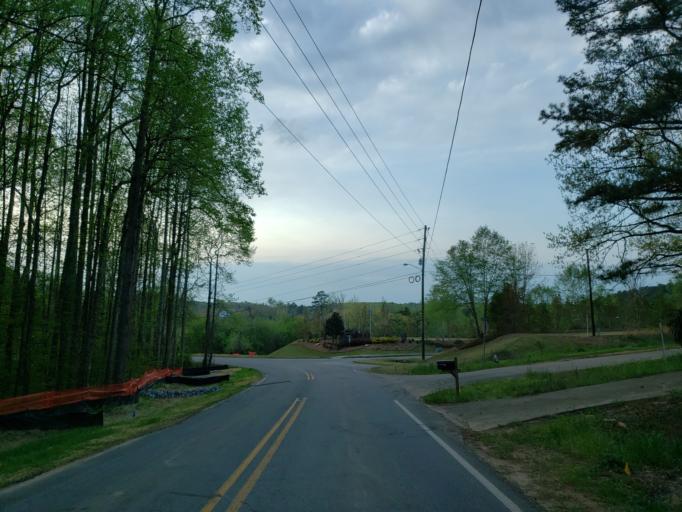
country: US
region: Georgia
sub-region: Cherokee County
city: Canton
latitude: 34.2916
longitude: -84.4601
